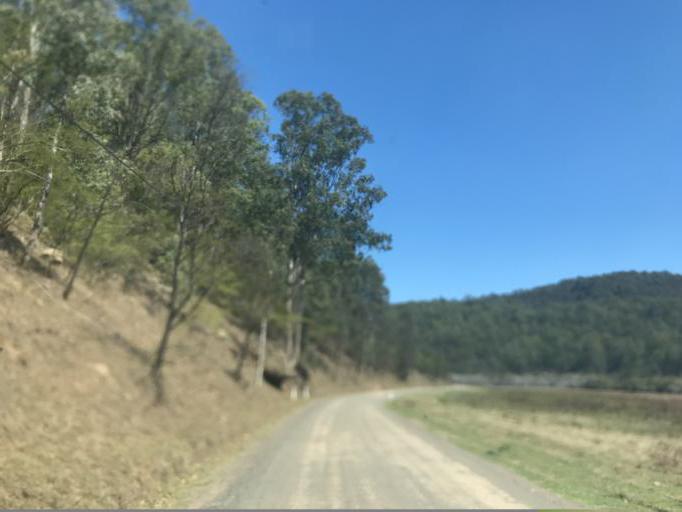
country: AU
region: New South Wales
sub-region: Hornsby Shire
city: Glenorie
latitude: -33.2461
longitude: 150.9783
